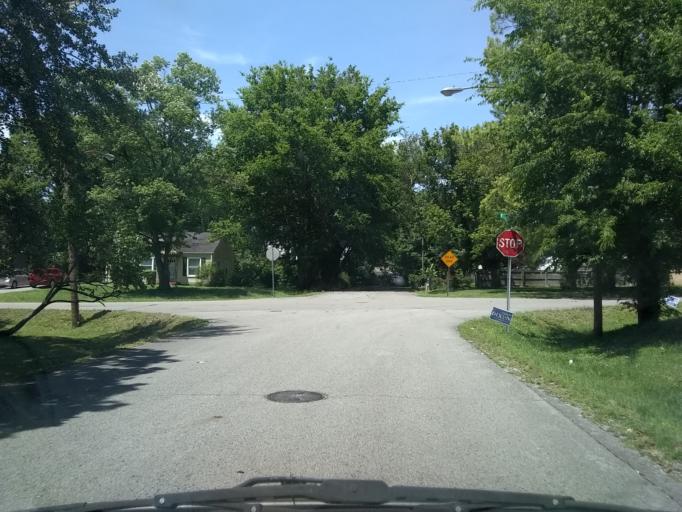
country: US
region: Tennessee
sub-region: Davidson County
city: Nashville
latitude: 36.1301
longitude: -86.7017
